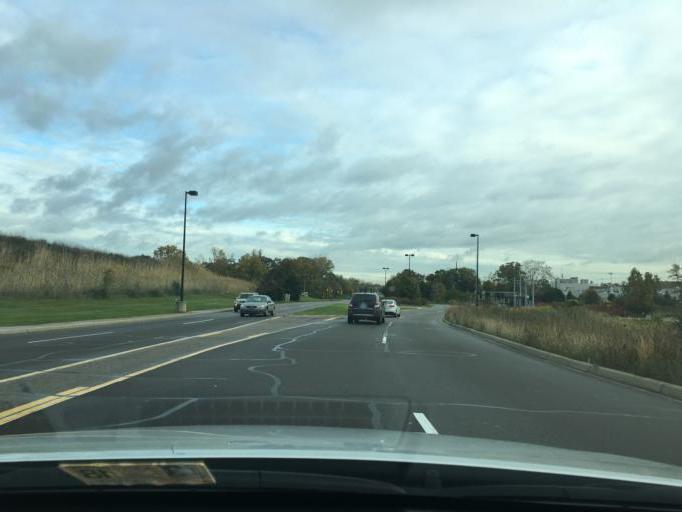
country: US
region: Michigan
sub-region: Wayne County
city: Melvindale
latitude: 42.2855
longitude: -83.2035
